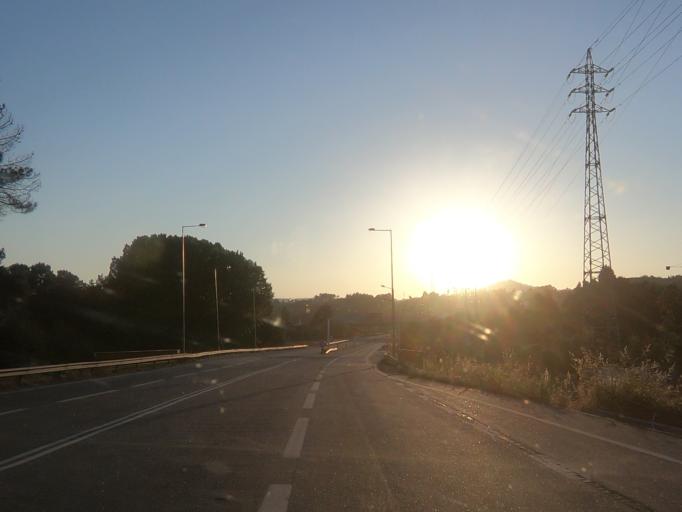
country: PT
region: Viseu
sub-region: Viseu
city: Rio de Loba
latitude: 40.6797
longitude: -7.8788
